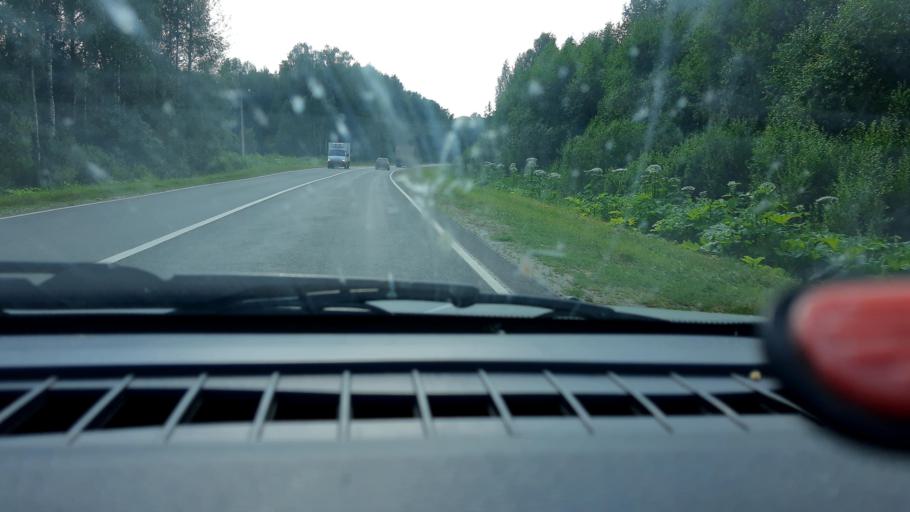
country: RU
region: Nizjnij Novgorod
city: Uren'
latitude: 57.2254
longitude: 45.5273
